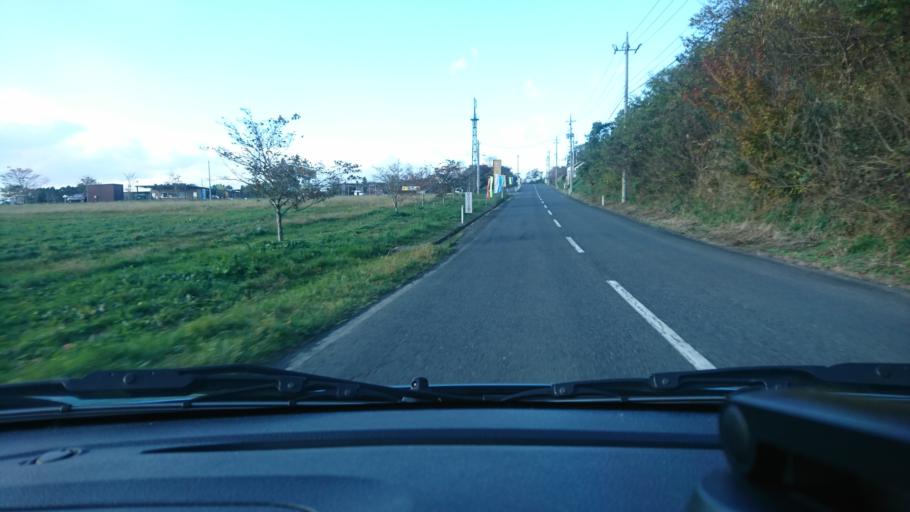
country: JP
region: Iwate
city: Ichinoseki
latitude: 38.8084
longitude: 141.2615
